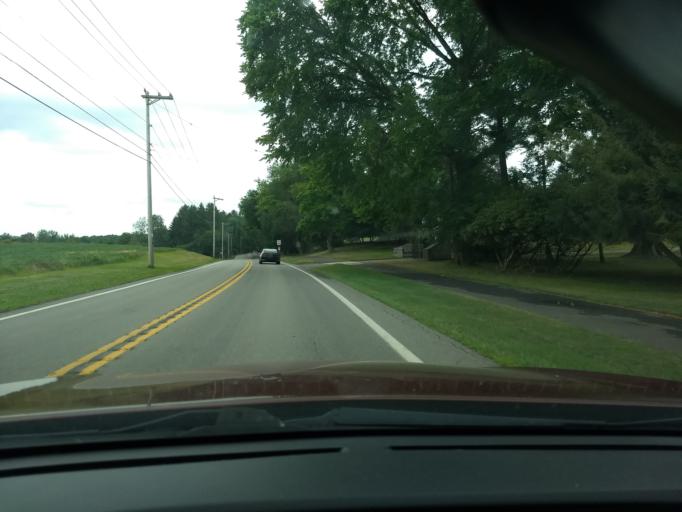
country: US
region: Pennsylvania
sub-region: Butler County
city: Mars
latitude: 40.6644
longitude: -80.0176
